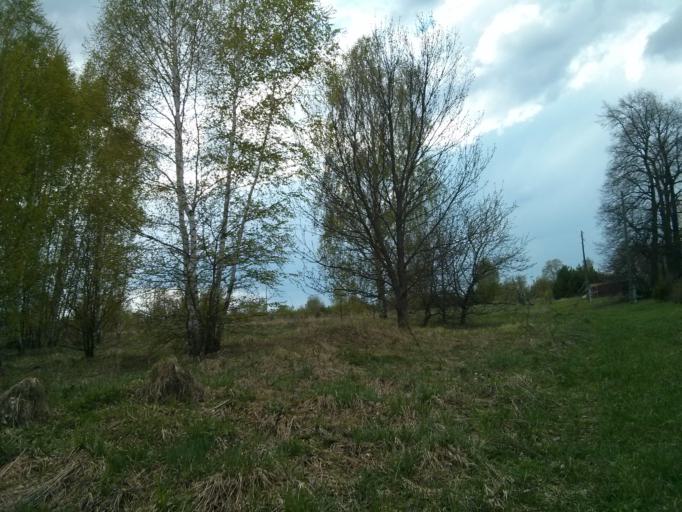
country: RU
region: Nizjnij Novgorod
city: Shimorskoye
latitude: 55.3070
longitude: 41.8431
